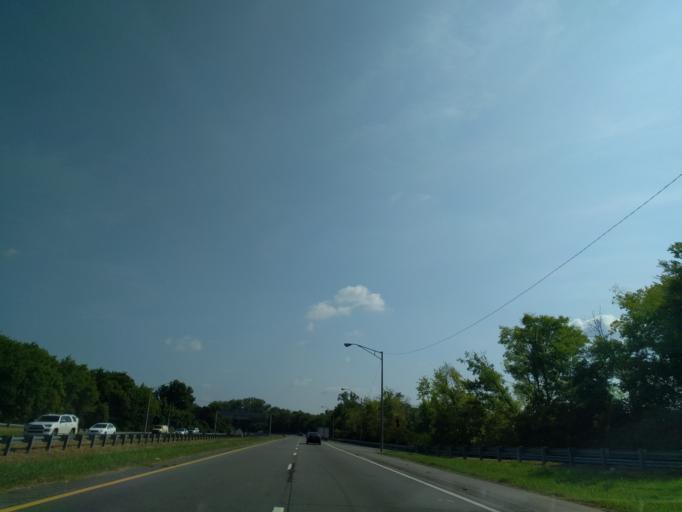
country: US
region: Tennessee
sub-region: Davidson County
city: Nashville
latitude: 36.1767
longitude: -86.7654
